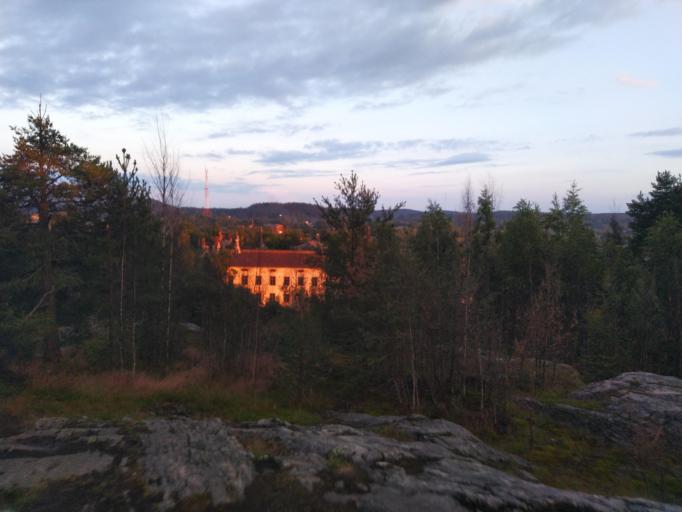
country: RU
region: Republic of Karelia
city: Sortavala
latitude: 61.7035
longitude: 30.6740
